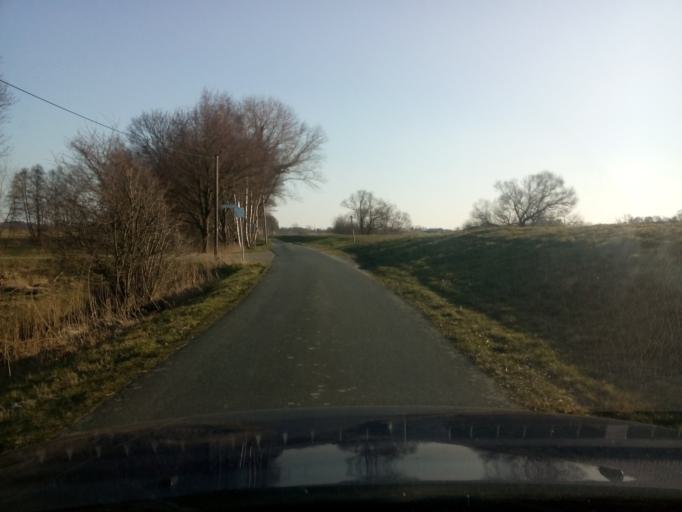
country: DE
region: Lower Saxony
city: Lilienthal
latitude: 53.1548
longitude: 8.8413
